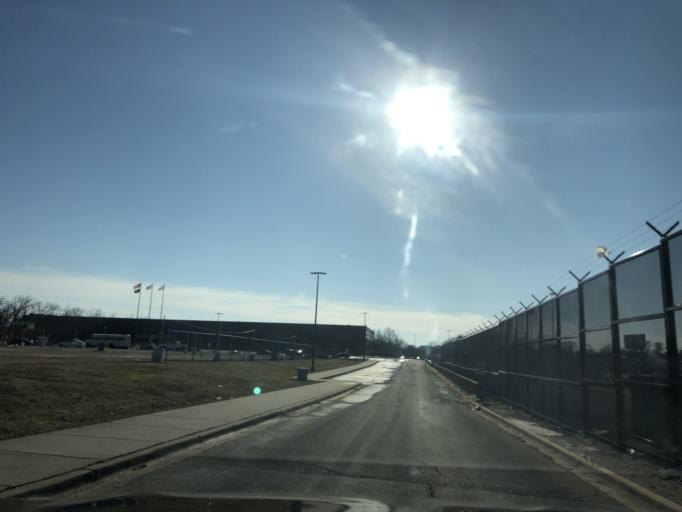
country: US
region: Illinois
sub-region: Cook County
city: Forest Park
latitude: 41.8750
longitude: -87.8276
